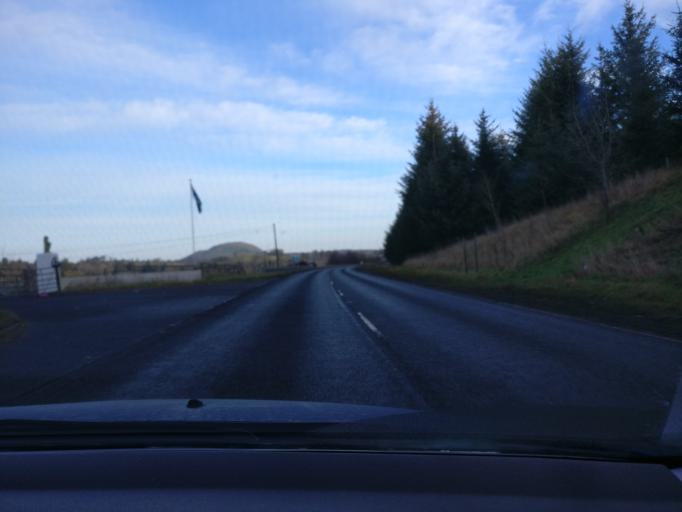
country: GB
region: Scotland
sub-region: The Scottish Borders
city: Hawick
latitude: 55.4467
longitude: -2.7288
